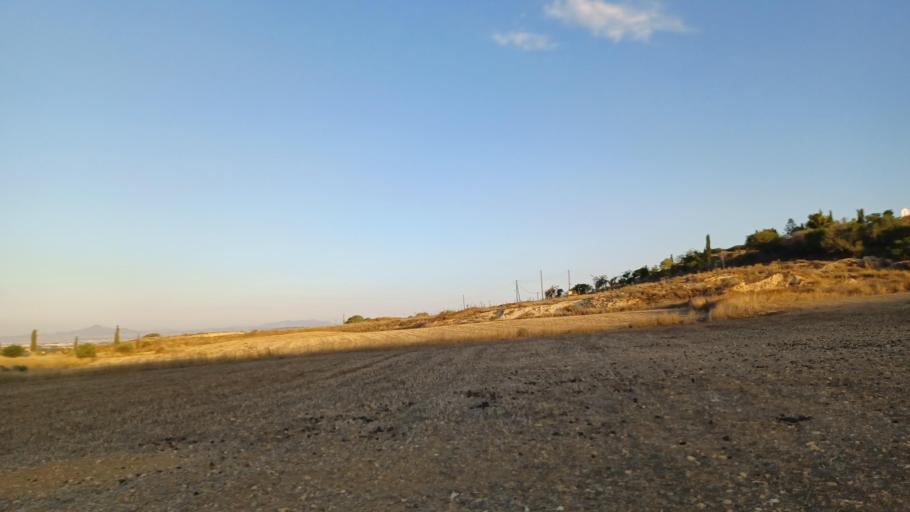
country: CY
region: Larnaka
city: Pyla
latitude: 34.9888
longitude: 33.7007
